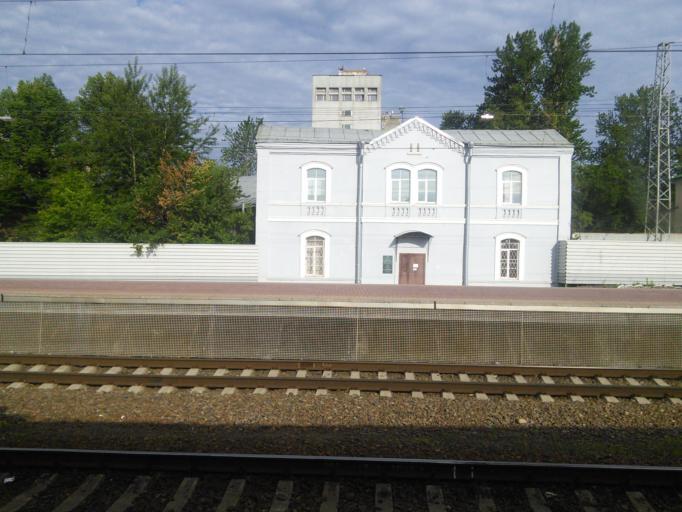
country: RU
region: Leningrad
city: Finlyandskiy
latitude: 59.9589
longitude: 30.3578
